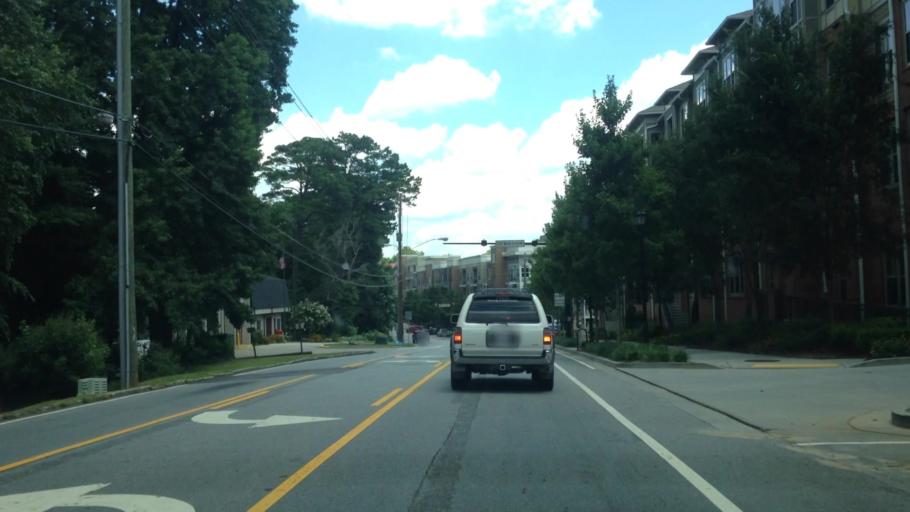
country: US
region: Georgia
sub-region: DeKalb County
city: North Atlanta
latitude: 33.8604
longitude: -84.3362
